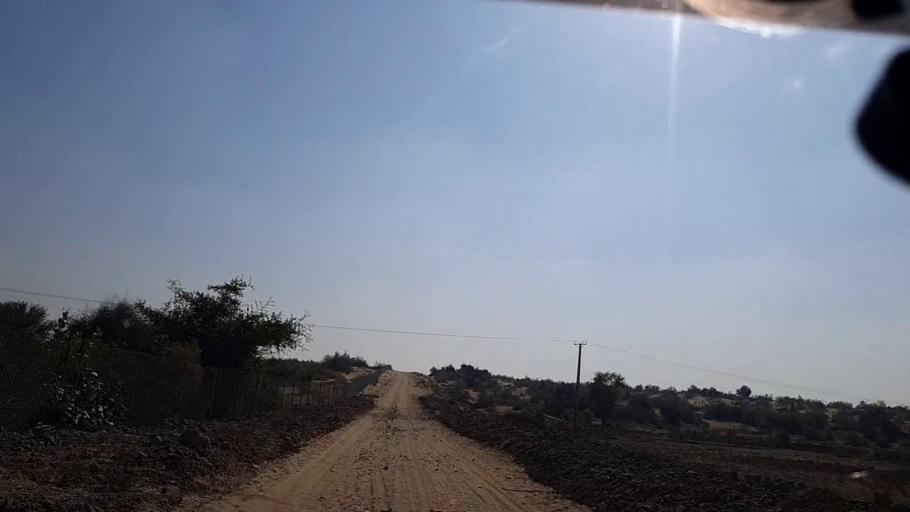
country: PK
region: Sindh
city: Khanpur
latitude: 27.5649
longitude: 69.3888
